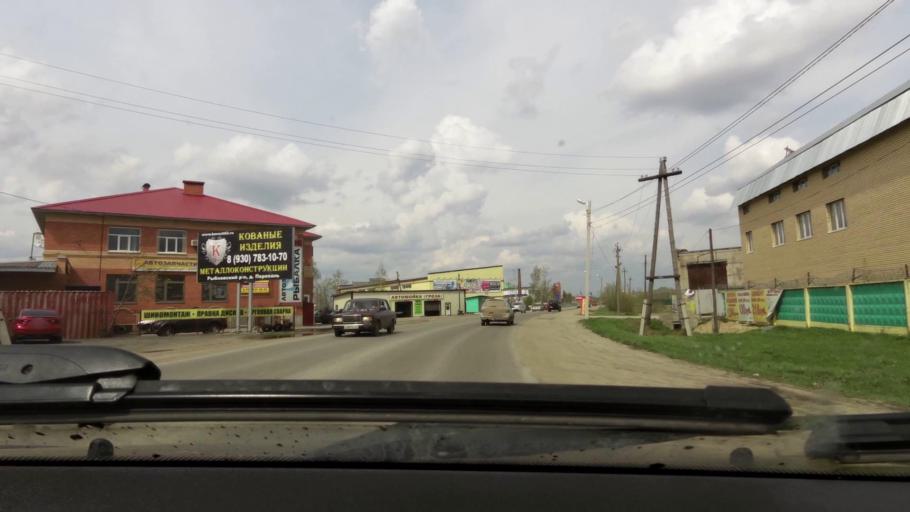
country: RU
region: Rjazan
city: Bagramovo
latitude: 54.7347
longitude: 39.4822
